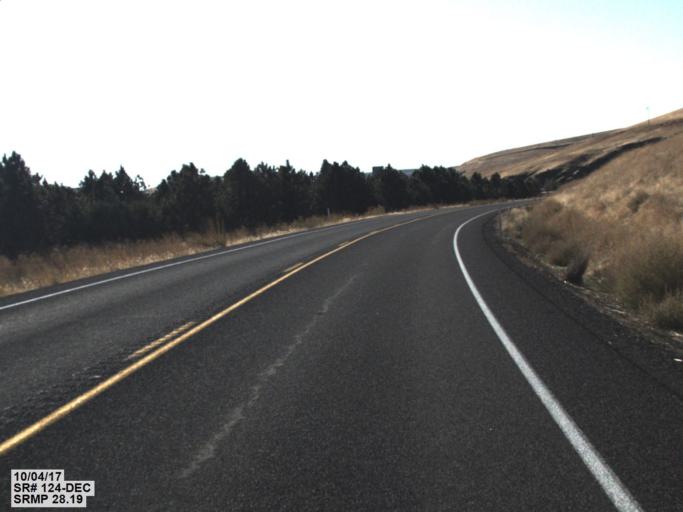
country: US
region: Washington
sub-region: Walla Walla County
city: Garrett
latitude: 46.2906
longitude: -118.4732
